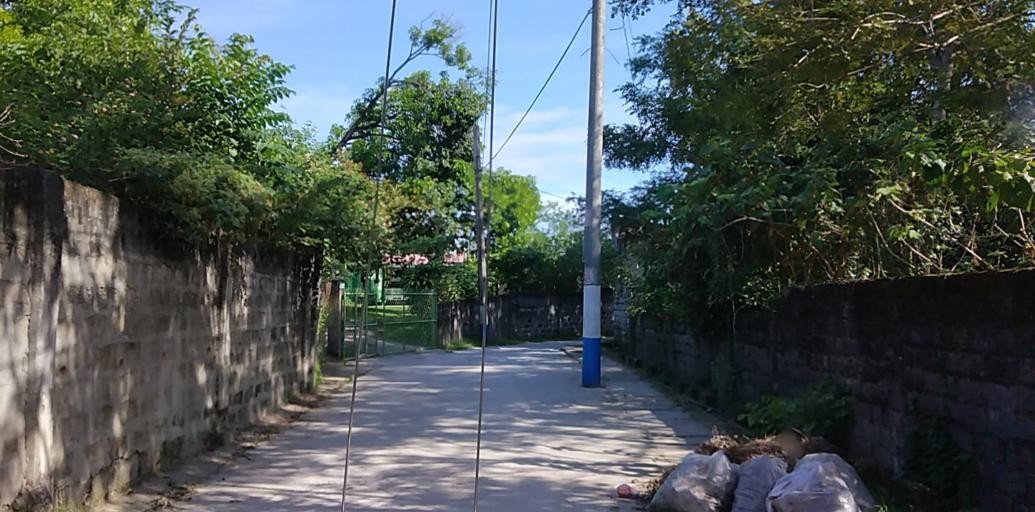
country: PH
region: Central Luzon
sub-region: Province of Pampanga
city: Porac
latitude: 15.0754
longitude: 120.5387
